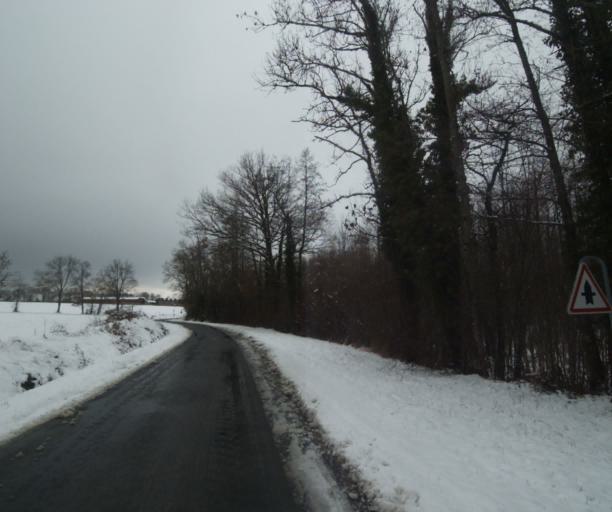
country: FR
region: Champagne-Ardenne
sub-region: Departement de la Haute-Marne
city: Laneuville-a-Remy
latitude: 48.4701
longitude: 4.8868
